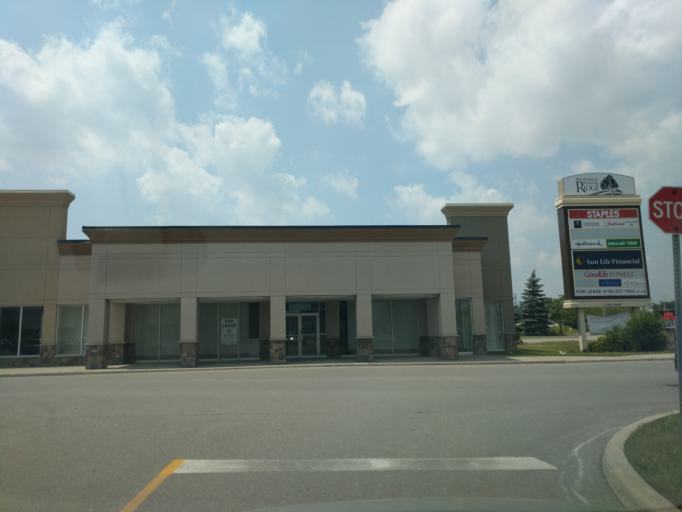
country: CA
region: Ontario
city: Ajax
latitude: 43.8429
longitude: -79.0680
